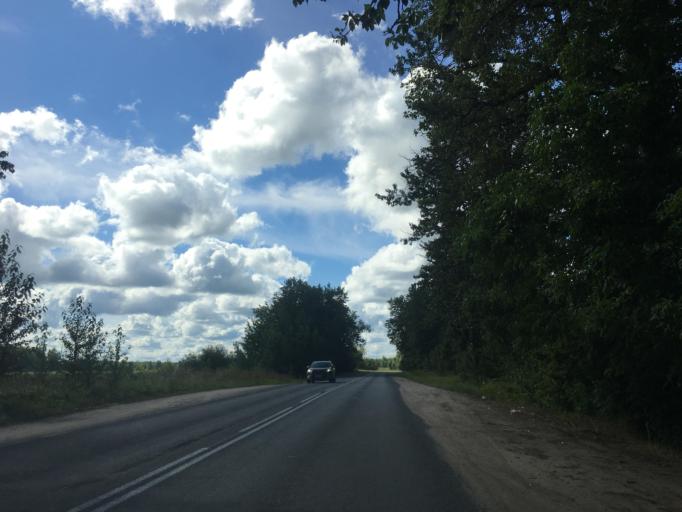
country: RU
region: Pskov
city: Pskov
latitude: 57.7808
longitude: 28.1688
